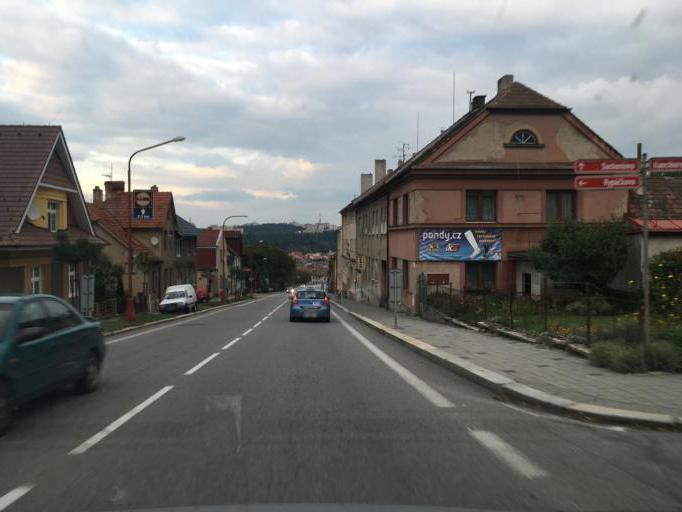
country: CZ
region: Vysocina
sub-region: Okres Trebic
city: Trebic
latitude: 49.2122
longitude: 15.8672
